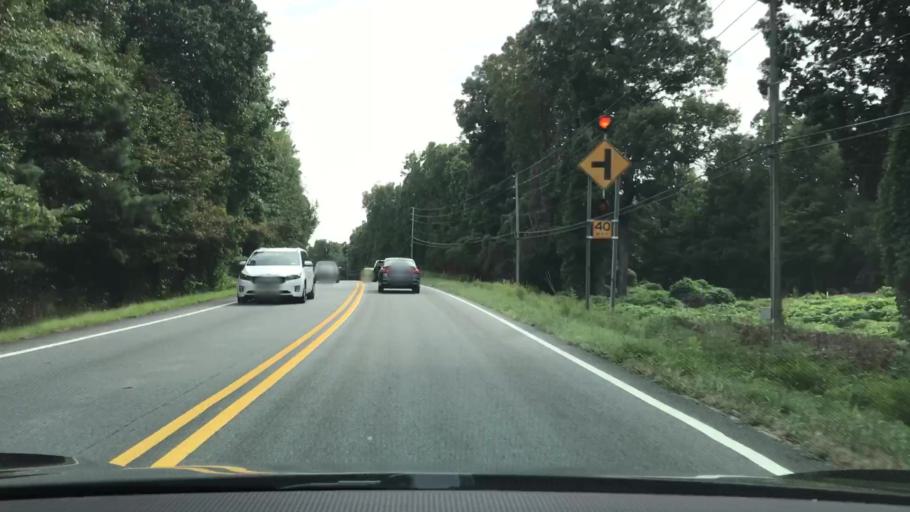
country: US
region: Georgia
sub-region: Gwinnett County
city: Suwanee
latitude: 34.0695
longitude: -84.0573
